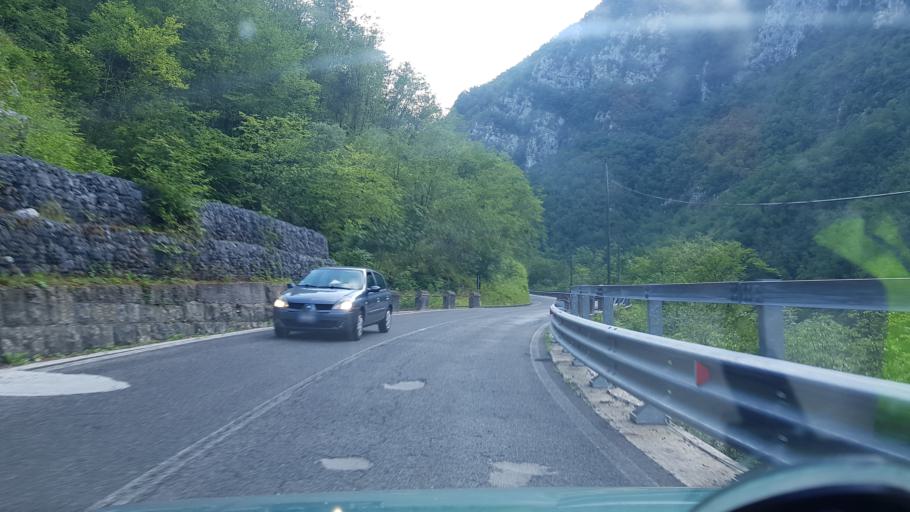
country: IT
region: Friuli Venezia Giulia
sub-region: Provincia di Udine
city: Lusevera
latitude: 46.2520
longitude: 13.2544
